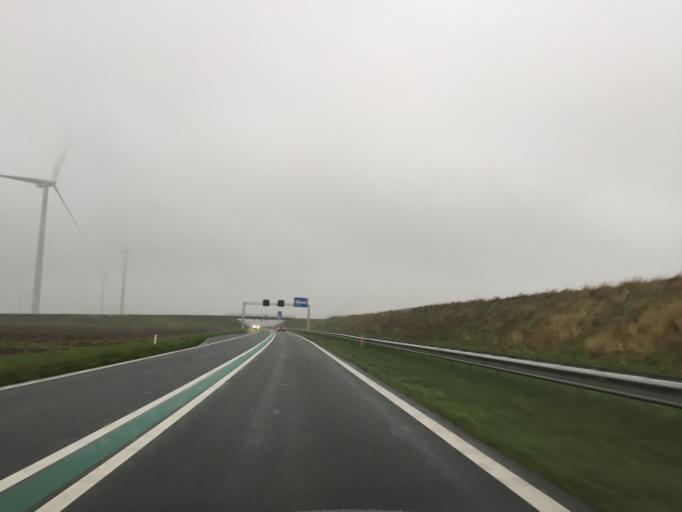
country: NL
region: Zeeland
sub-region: Gemeente Terneuzen
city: Sluiskil
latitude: 51.2838
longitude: 3.8733
